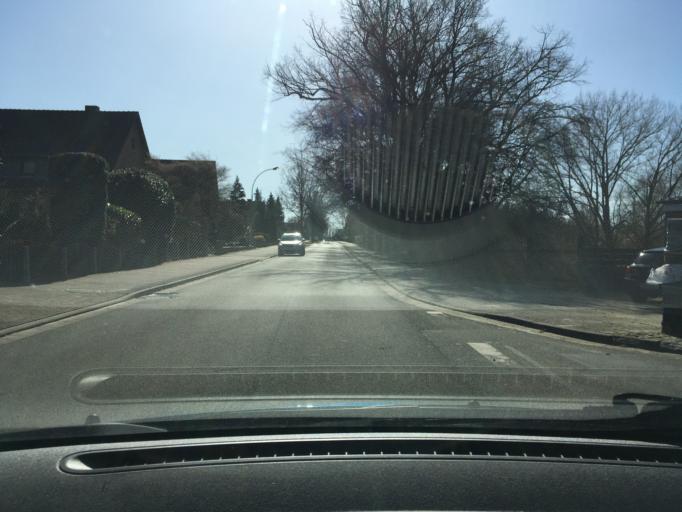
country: DE
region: Lower Saxony
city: Ebstorf
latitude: 53.0246
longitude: 10.4094
